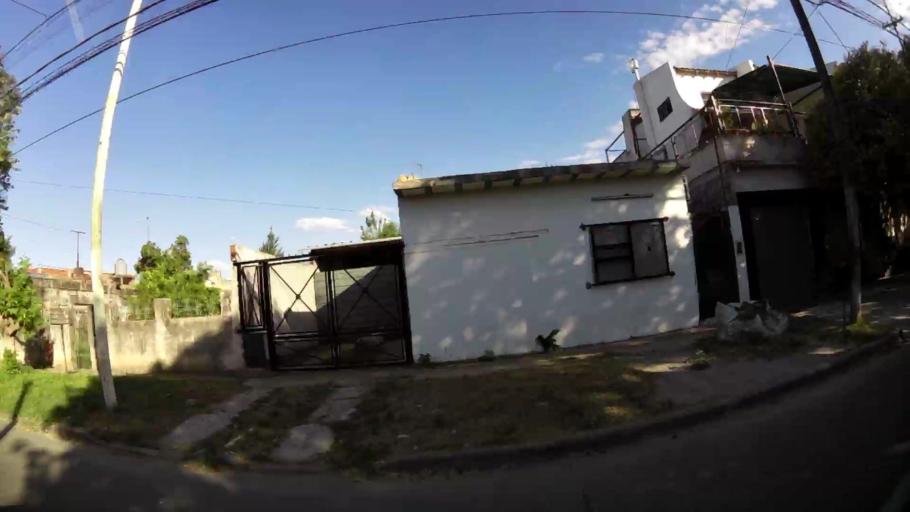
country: AR
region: Buenos Aires
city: Hurlingham
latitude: -34.5702
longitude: -58.6126
